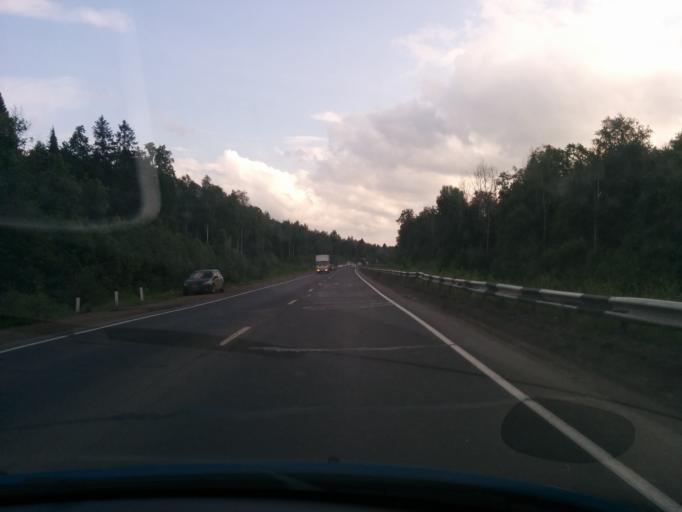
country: RU
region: Perm
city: Novyye Lyady
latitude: 58.0751
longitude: 56.4315
